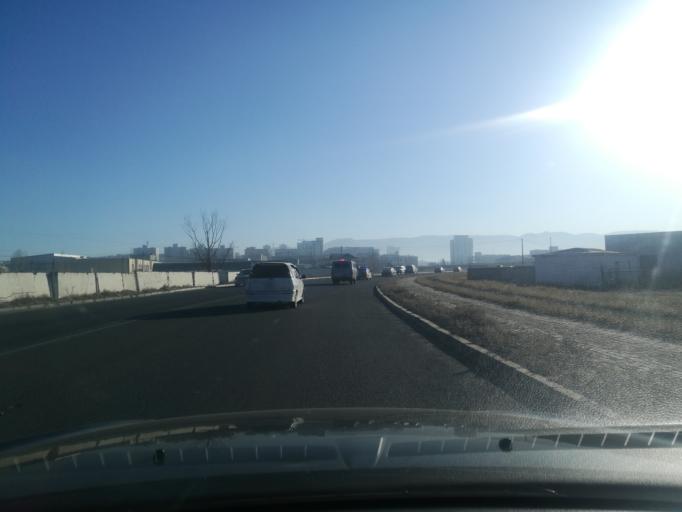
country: MN
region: Ulaanbaatar
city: Ulaanbaatar
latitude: 47.8569
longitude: 106.7513
